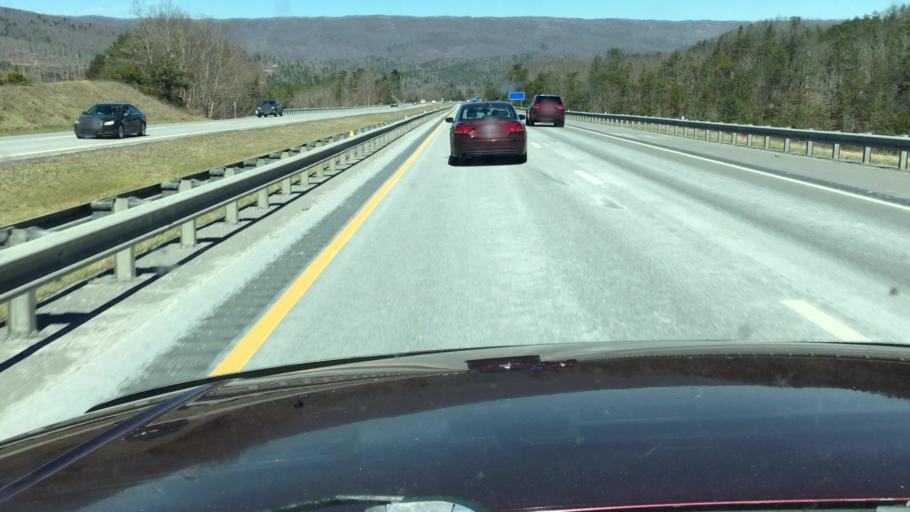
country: US
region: Virginia
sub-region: Bland County
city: Bland
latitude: 37.1465
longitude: -81.1393
